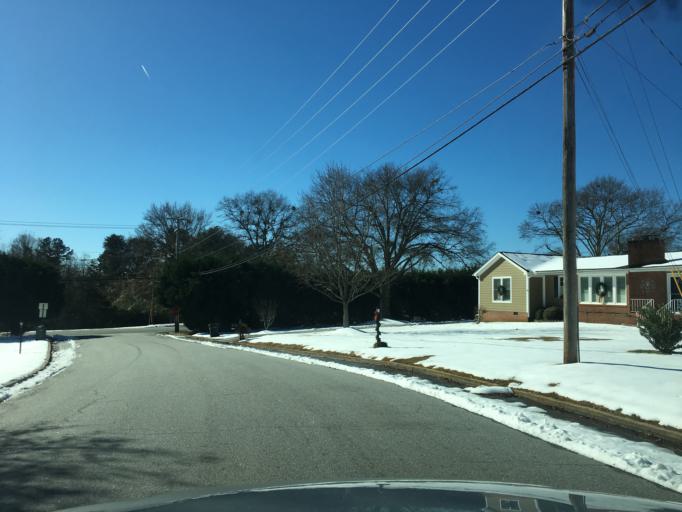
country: US
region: South Carolina
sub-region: Greenville County
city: Greer
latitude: 34.9454
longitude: -82.2578
